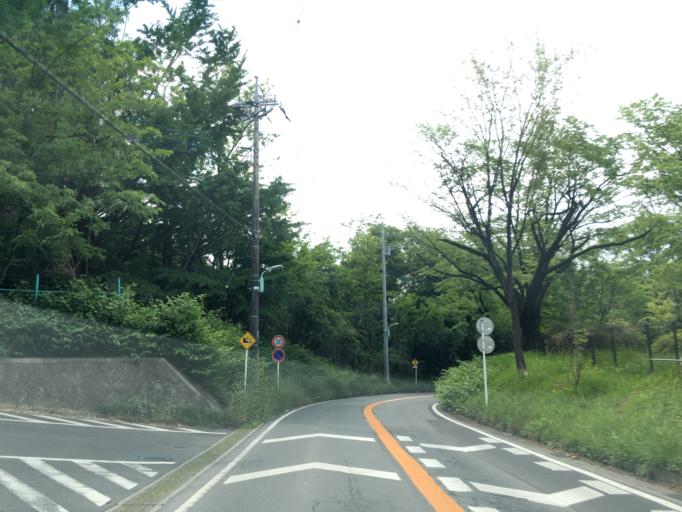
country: JP
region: Saitama
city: Tokorozawa
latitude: 35.7835
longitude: 139.4158
